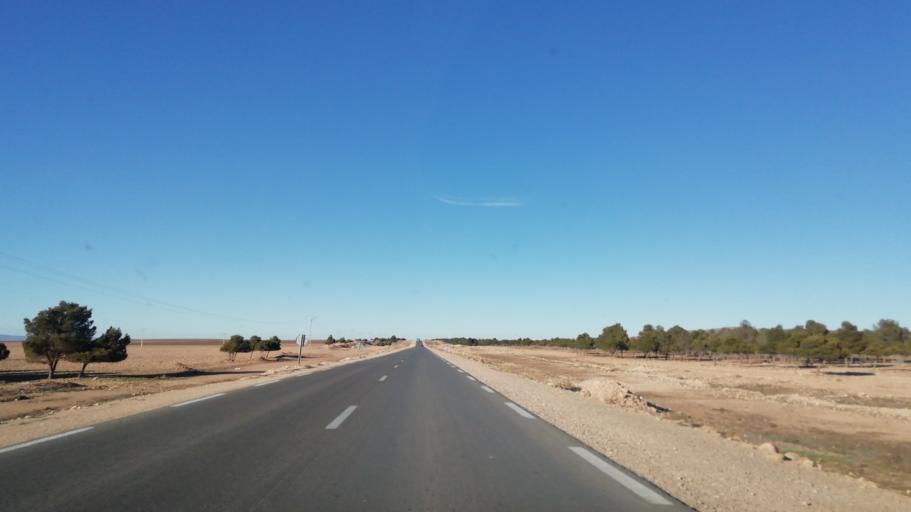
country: DZ
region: Tlemcen
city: Sebdou
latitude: 34.2356
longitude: -1.2566
